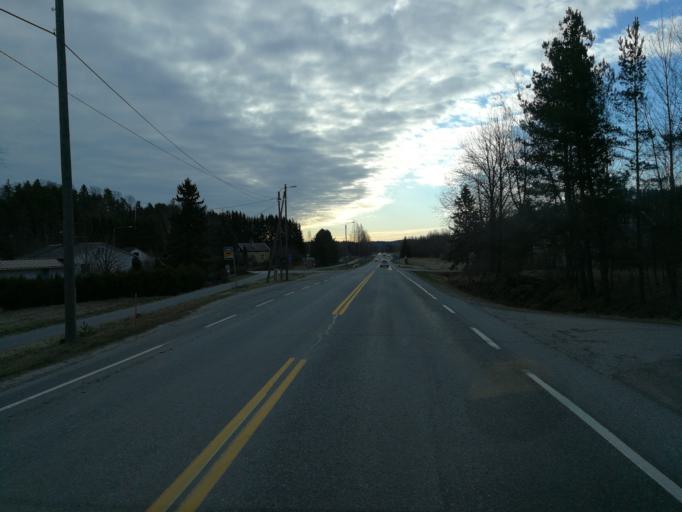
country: FI
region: Varsinais-Suomi
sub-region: Turku
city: Piikkioe
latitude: 60.4207
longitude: 22.4650
